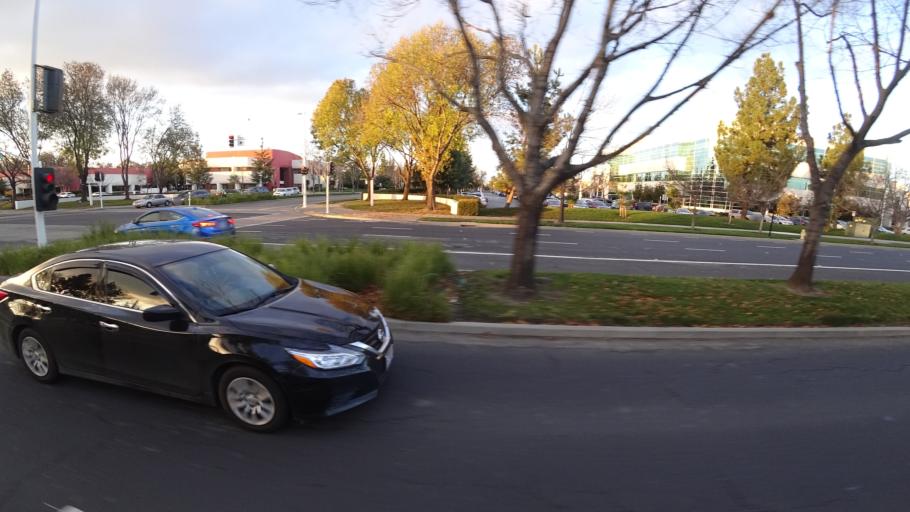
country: US
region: California
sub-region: Alameda County
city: Pleasanton
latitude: 37.6913
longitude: -121.8982
